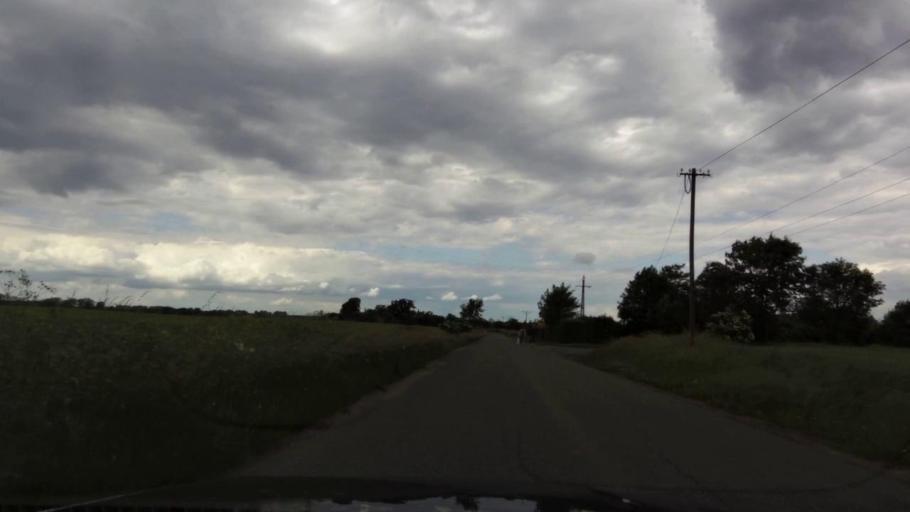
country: PL
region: West Pomeranian Voivodeship
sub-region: Powiat mysliborski
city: Mysliborz
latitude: 52.9549
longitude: 14.7914
